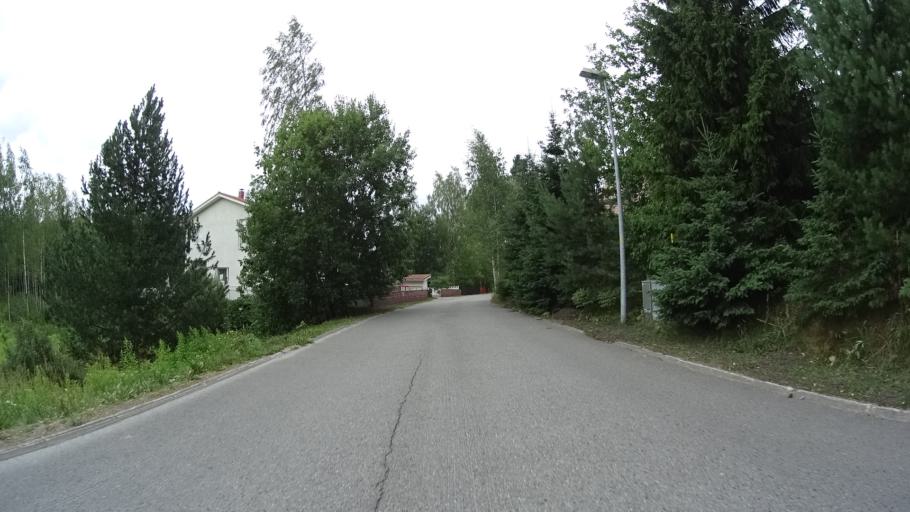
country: FI
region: Uusimaa
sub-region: Helsinki
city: Espoo
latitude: 60.1353
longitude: 24.6792
